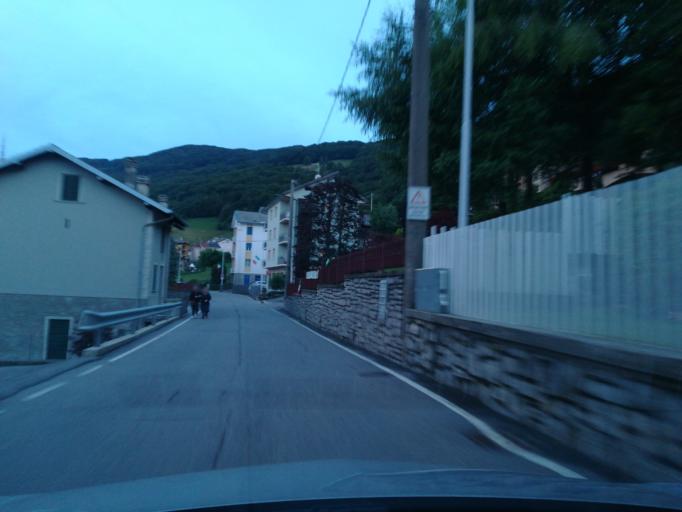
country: IT
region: Lombardy
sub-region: Provincia di Bergamo
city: Costa Valle Imagna
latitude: 45.8043
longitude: 9.5024
